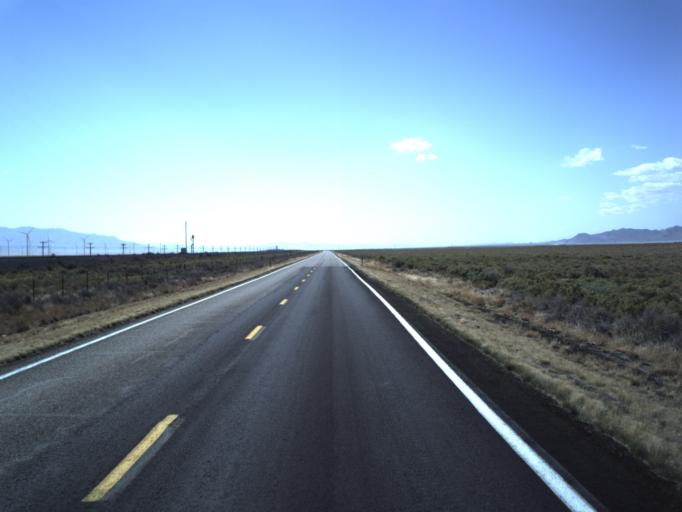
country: US
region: Utah
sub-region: Beaver County
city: Milford
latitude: 38.6221
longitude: -112.9850
